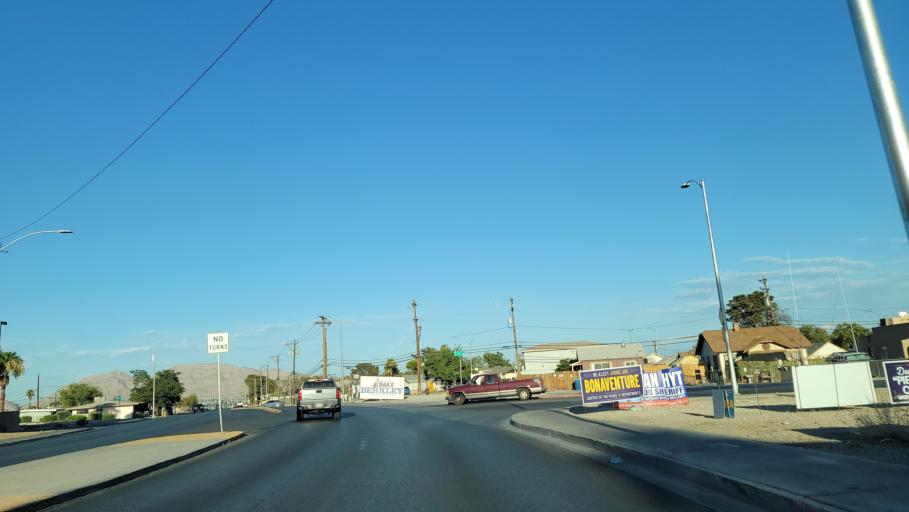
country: US
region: Nevada
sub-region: Clark County
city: Las Vegas
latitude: 36.1741
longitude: -115.1354
